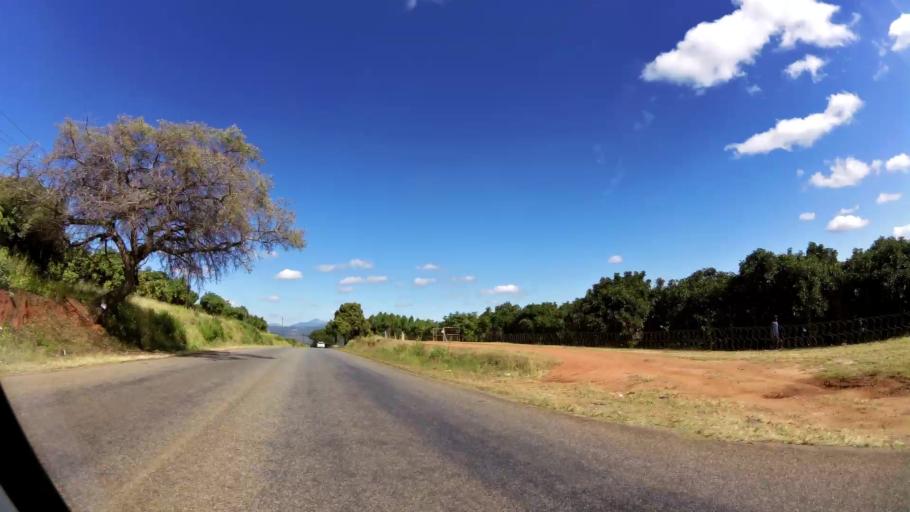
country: ZA
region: Limpopo
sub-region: Mopani District Municipality
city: Tzaneen
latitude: -23.8059
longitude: 30.1779
